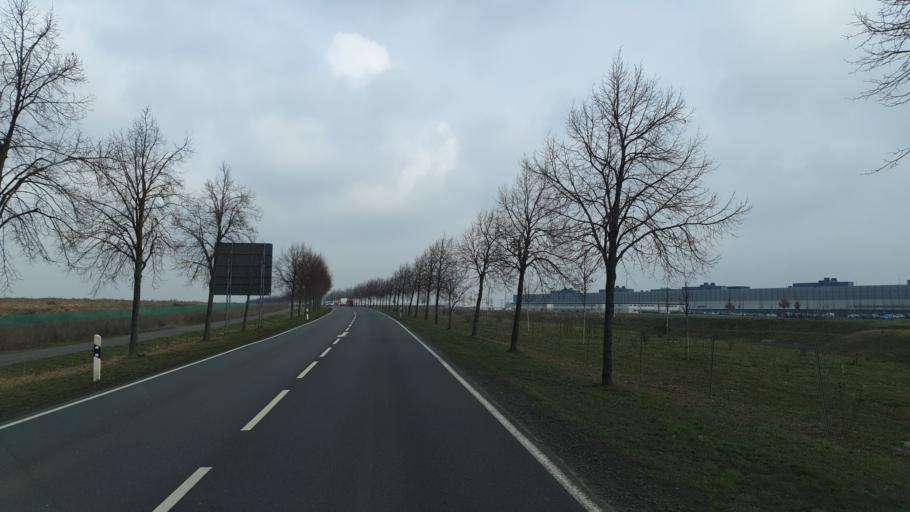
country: DE
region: Saxony
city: Schkeuditz
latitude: 51.4025
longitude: 12.2780
